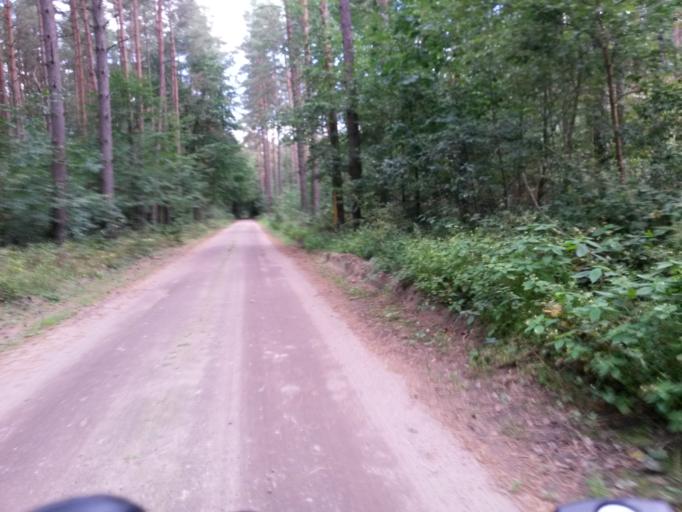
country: DE
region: Brandenburg
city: Templin
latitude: 53.1734
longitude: 13.4915
